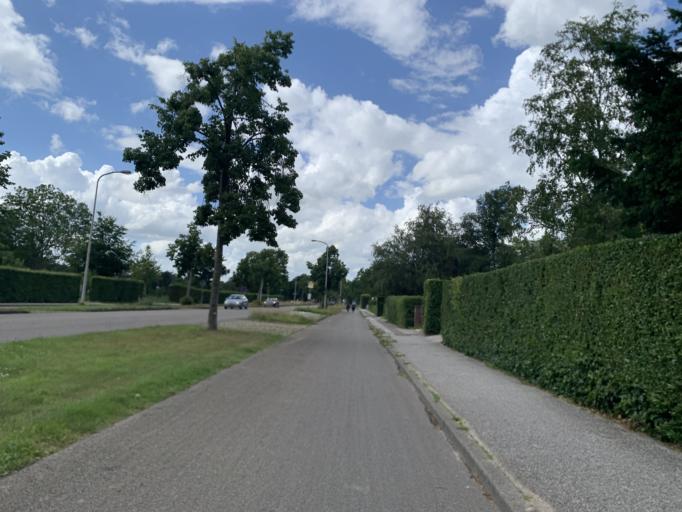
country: NL
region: Groningen
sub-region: Gemeente Haren
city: Haren
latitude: 53.1848
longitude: 6.5891
